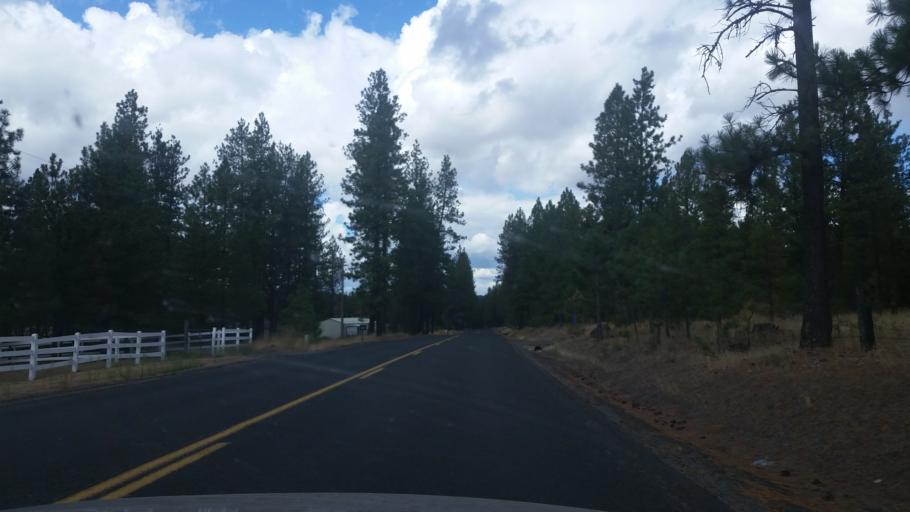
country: US
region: Washington
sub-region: Spokane County
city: Cheney
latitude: 47.5471
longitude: -117.4822
